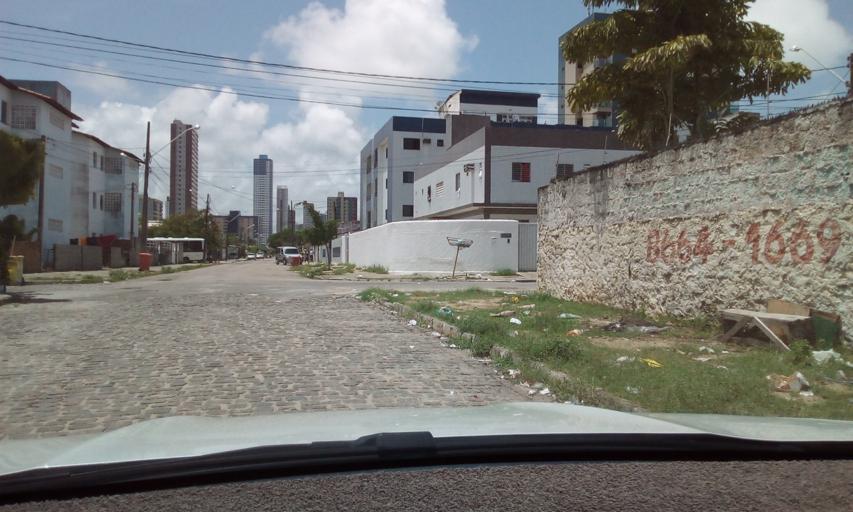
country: BR
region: Paraiba
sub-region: Joao Pessoa
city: Joao Pessoa
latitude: -7.1100
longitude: -34.8367
